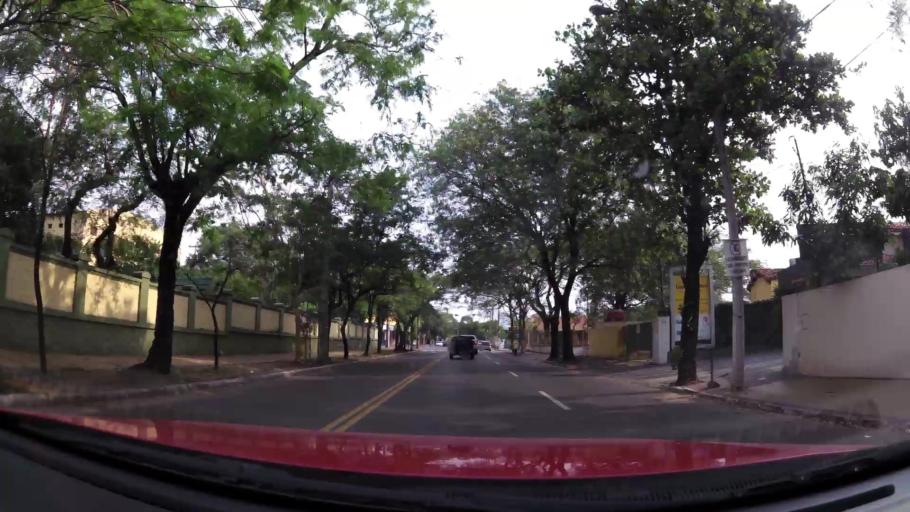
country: PY
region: Asuncion
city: Asuncion
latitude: -25.2964
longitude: -57.6119
